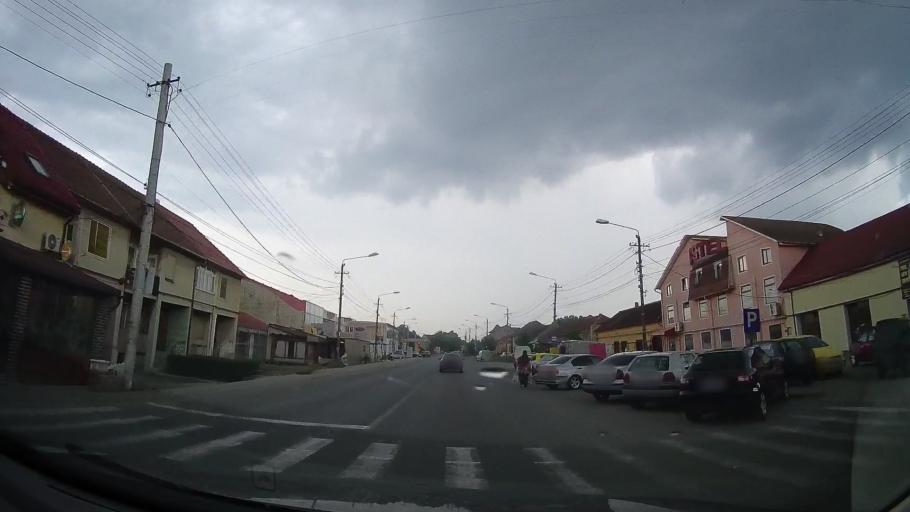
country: RO
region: Caras-Severin
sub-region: Municipiul Caransebes
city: Caransebes
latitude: 45.4070
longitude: 22.2229
